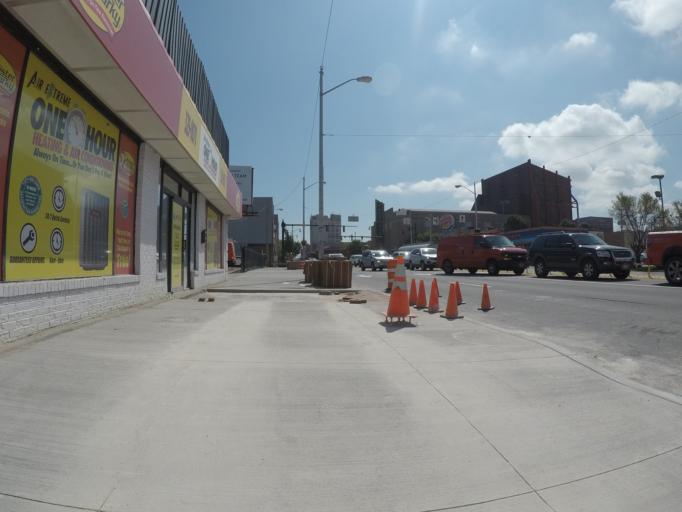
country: US
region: Kentucky
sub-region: Boyd County
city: Ashland
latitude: 38.4809
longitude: -82.6437
